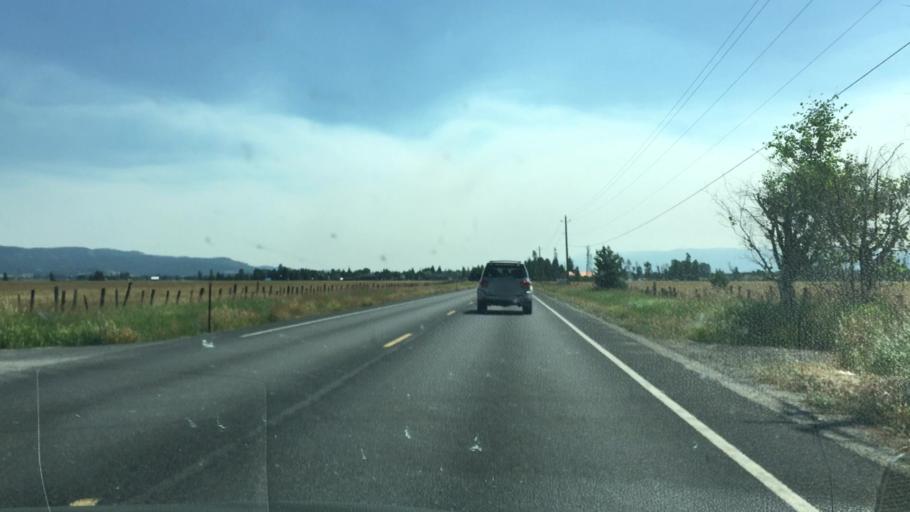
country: US
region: Idaho
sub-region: Valley County
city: McCall
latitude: 44.7456
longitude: -116.0783
